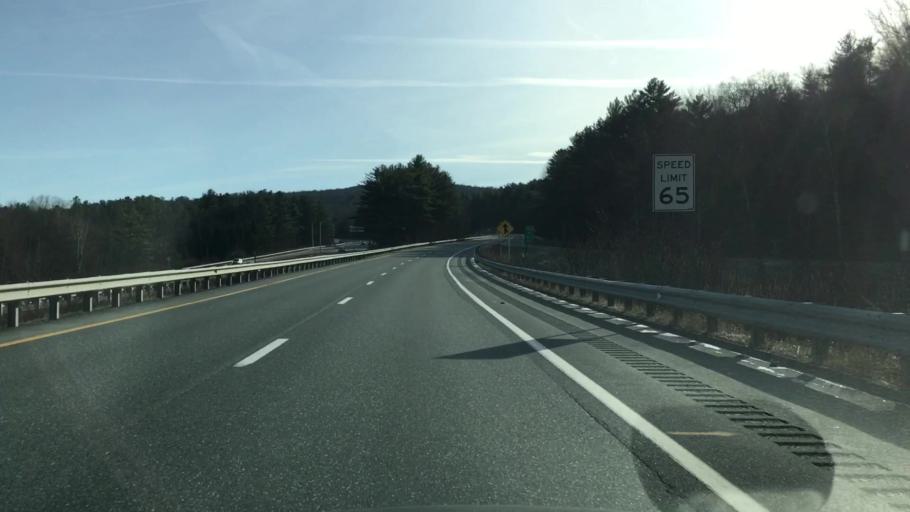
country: US
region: New Hampshire
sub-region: Grafton County
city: Lebanon
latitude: 43.6341
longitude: -72.2117
